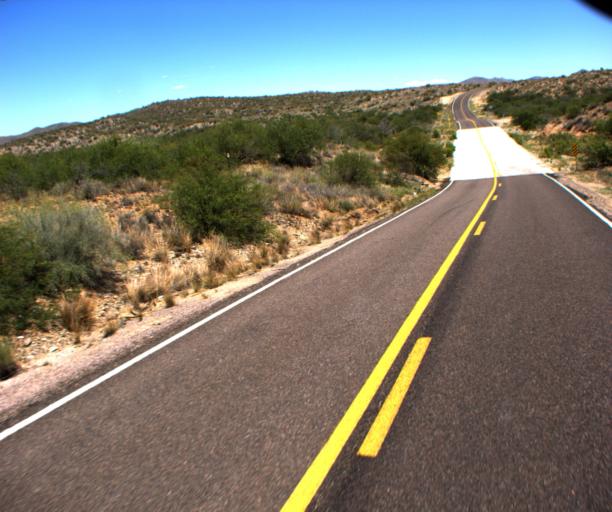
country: US
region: Arizona
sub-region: Yavapai County
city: Bagdad
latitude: 34.4968
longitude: -113.1756
